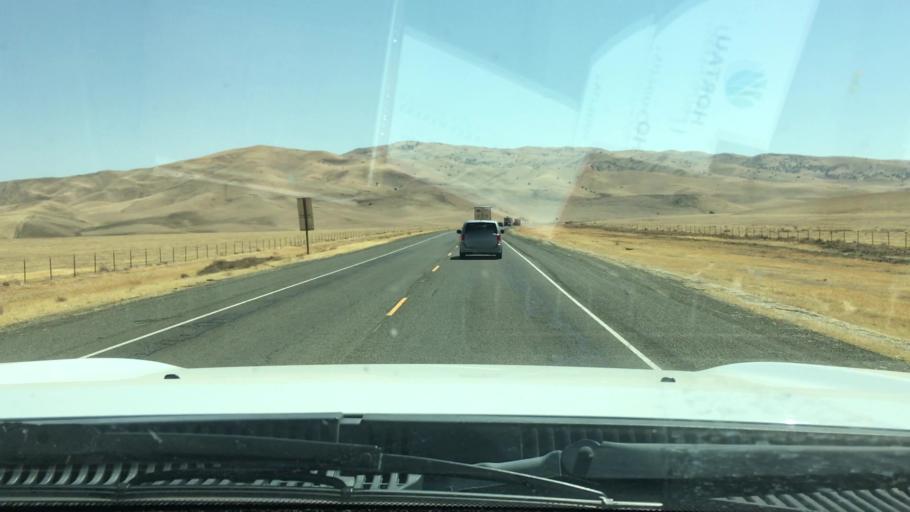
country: US
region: California
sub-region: Kings County
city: Avenal
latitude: 35.7954
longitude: -120.1075
